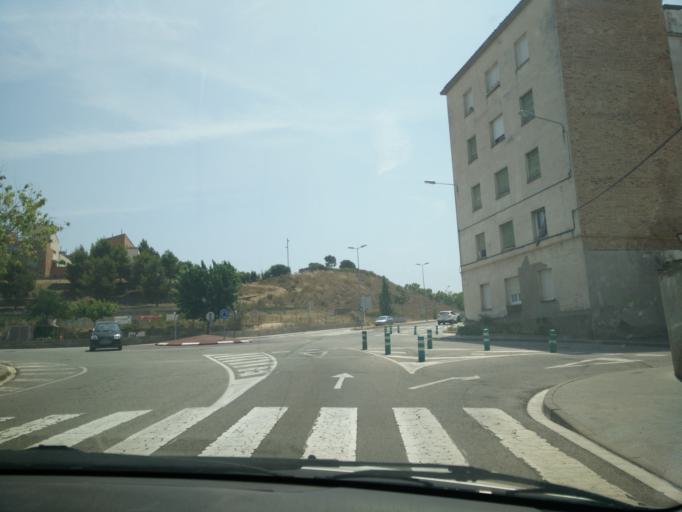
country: ES
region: Catalonia
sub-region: Provincia de Barcelona
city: Manresa
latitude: 41.7229
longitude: 1.8408
